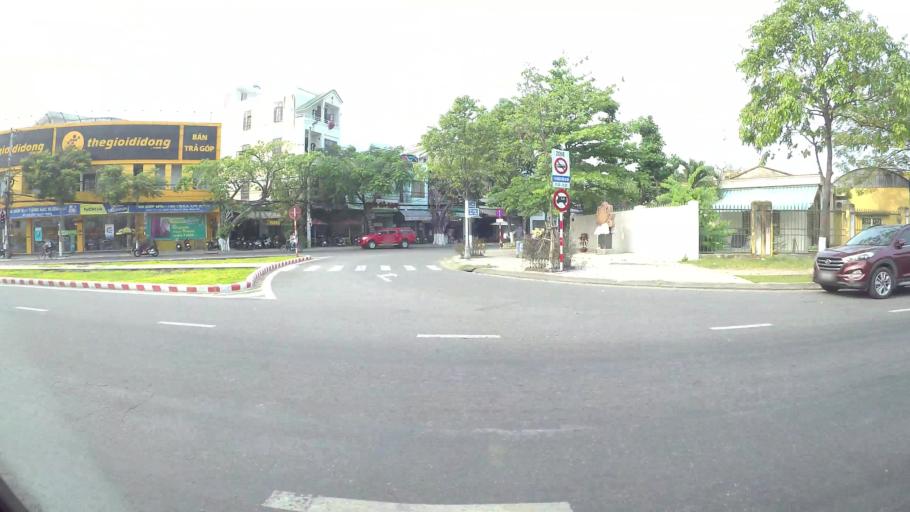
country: VN
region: Da Nang
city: Da Nang
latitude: 16.0485
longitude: 108.2134
